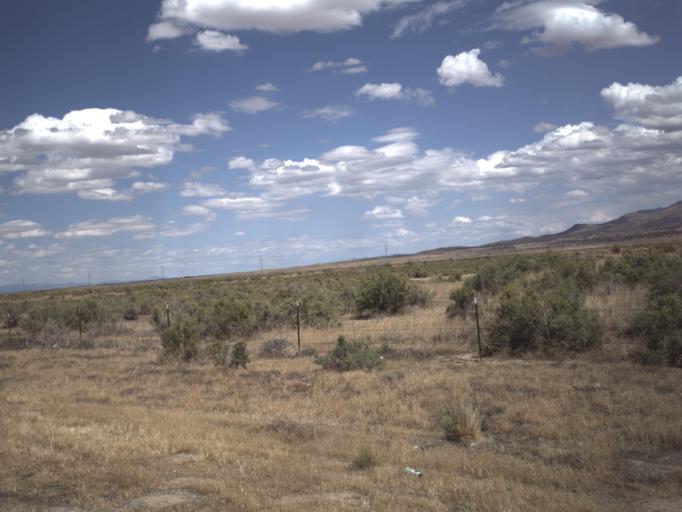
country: US
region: Utah
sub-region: Millard County
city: Delta
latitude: 39.2337
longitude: -112.4288
